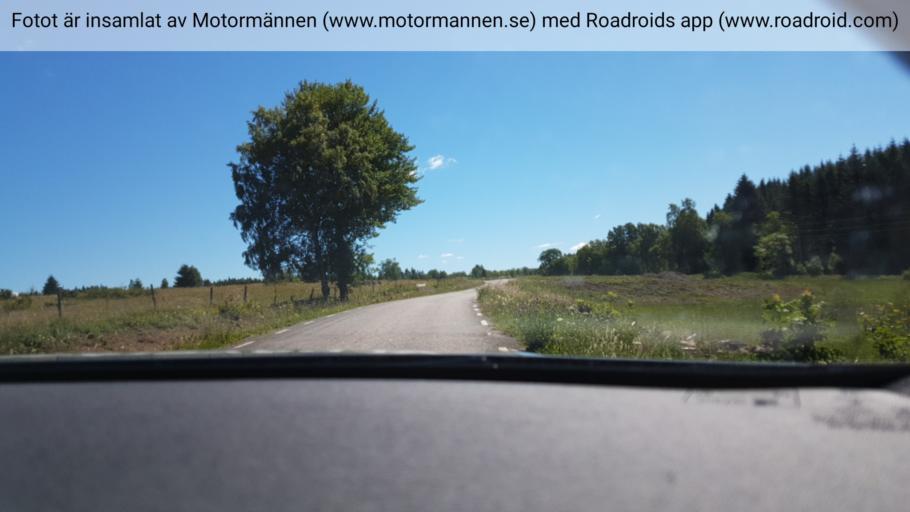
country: SE
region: Vaestra Goetaland
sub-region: Falkopings Kommun
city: Akarp
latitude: 58.1874
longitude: 13.7558
